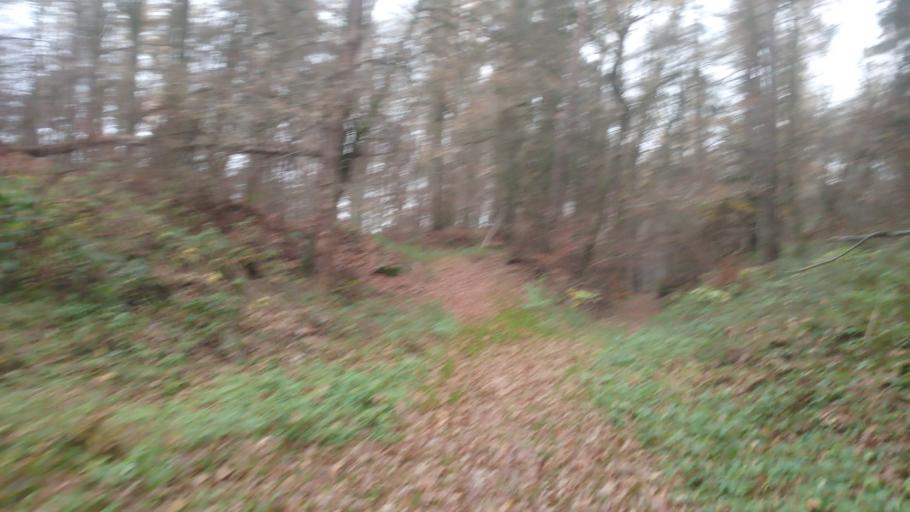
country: DE
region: North Rhine-Westphalia
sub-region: Regierungsbezirk Detmold
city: Willebadessen
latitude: 51.5082
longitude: 9.0073
